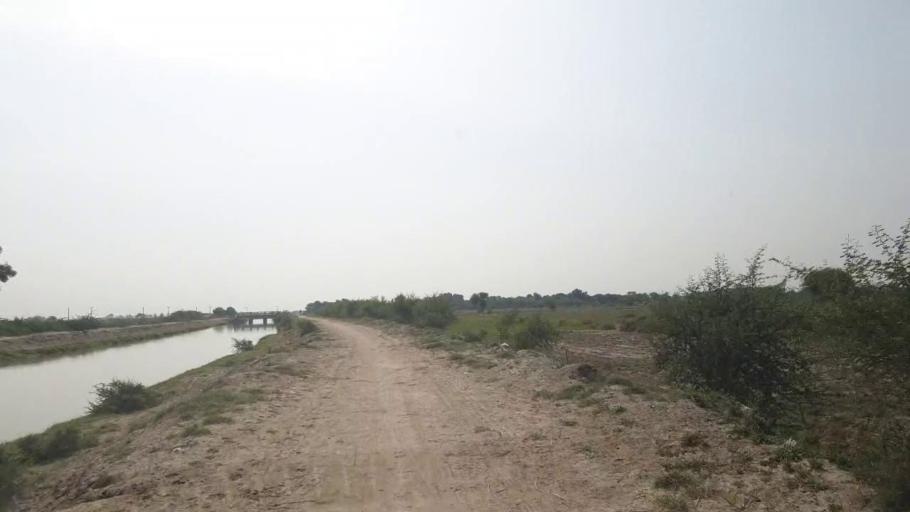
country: PK
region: Sindh
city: Badin
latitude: 24.5556
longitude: 68.8495
